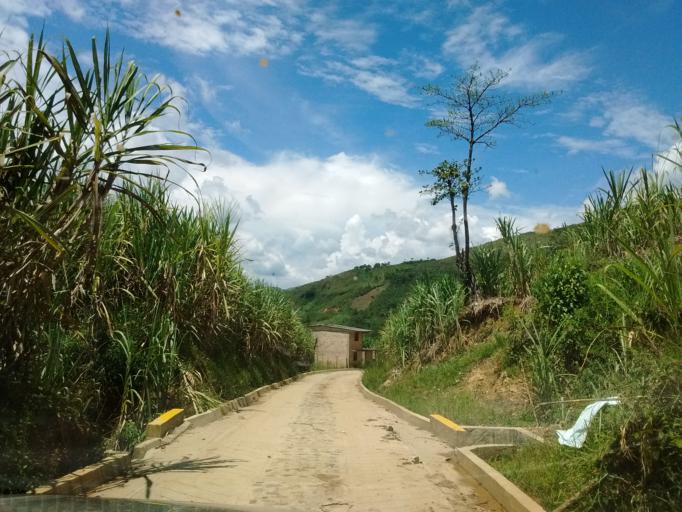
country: CO
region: Cauca
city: Villa Rica
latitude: 2.6286
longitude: -76.7723
